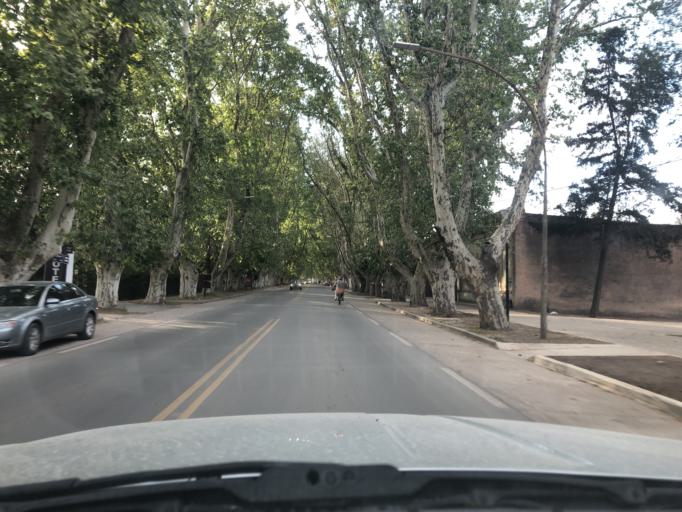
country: AR
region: Cordoba
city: Jesus Maria
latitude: -30.9977
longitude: -64.0893
